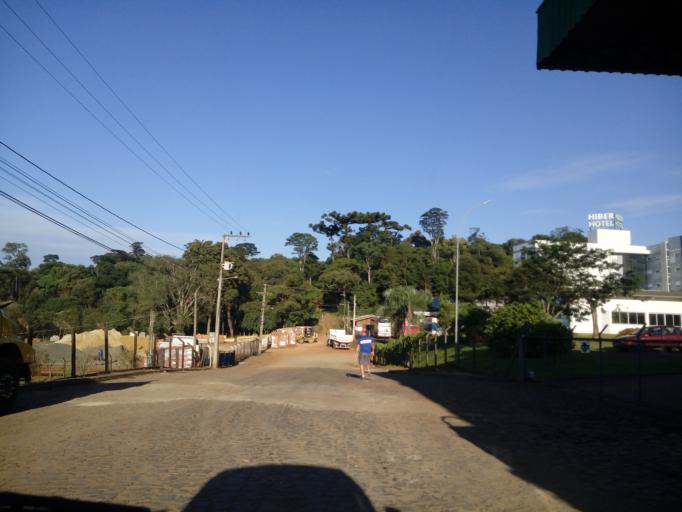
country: BR
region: Santa Catarina
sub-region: Chapeco
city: Chapeco
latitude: -27.0019
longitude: -52.6462
